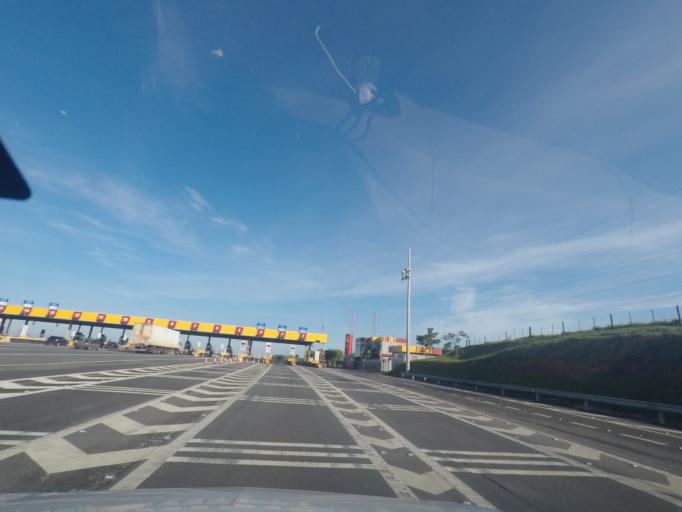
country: BR
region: Sao Paulo
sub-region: Nova Odessa
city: Nova Odessa
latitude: -22.7710
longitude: -47.2379
